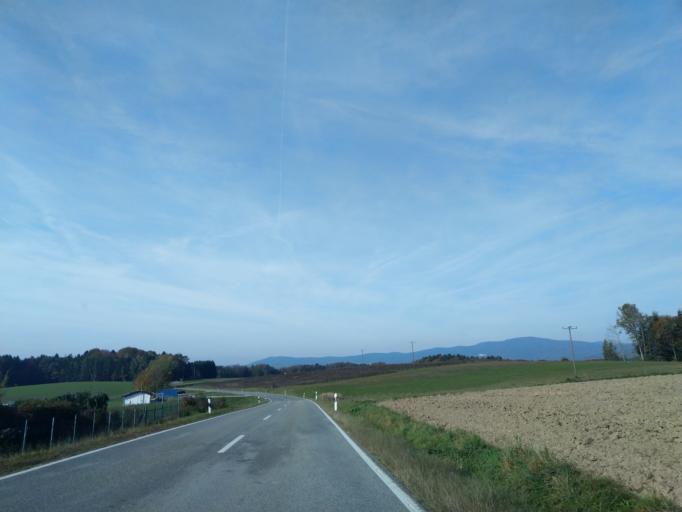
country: DE
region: Bavaria
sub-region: Lower Bavaria
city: Grattersdorf
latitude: 48.8083
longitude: 13.1416
